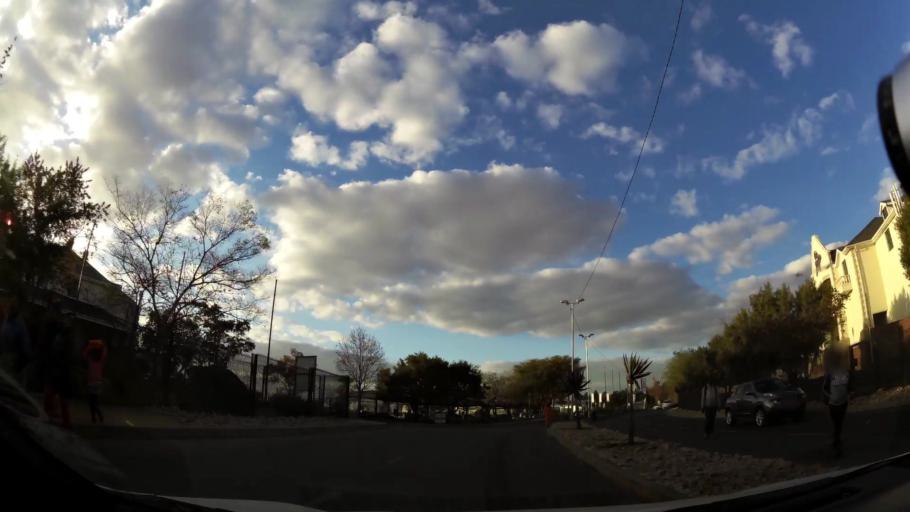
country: ZA
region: Gauteng
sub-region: City of Johannesburg Metropolitan Municipality
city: Diepsloot
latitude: -26.0023
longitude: 27.9836
